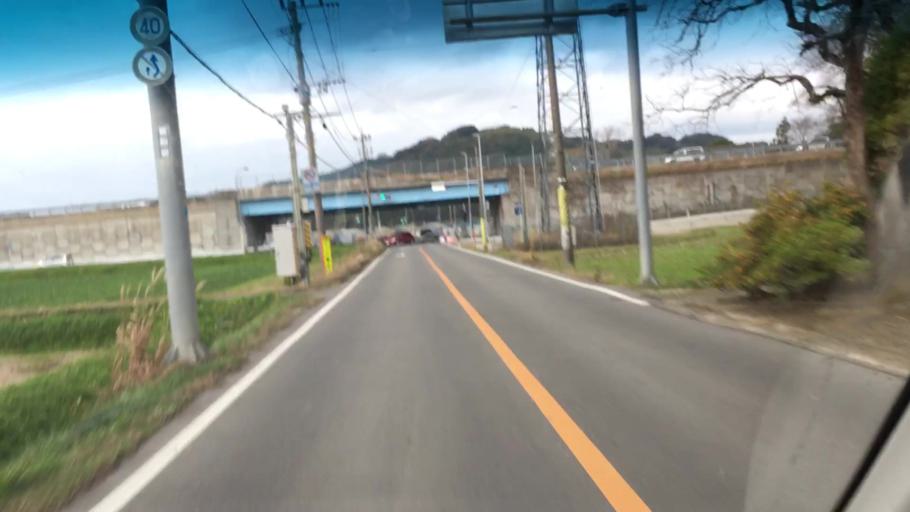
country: JP
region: Fukuoka
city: Maebaru-chuo
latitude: 33.5306
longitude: 130.1883
